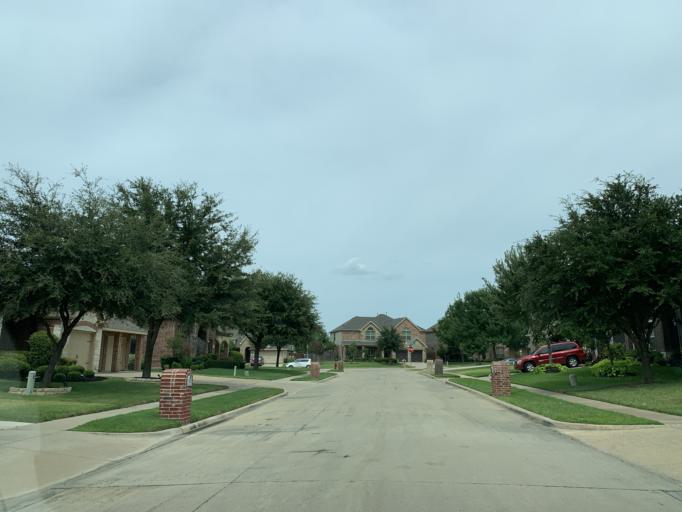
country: US
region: Texas
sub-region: Dallas County
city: Grand Prairie
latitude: 32.6572
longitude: -97.0376
